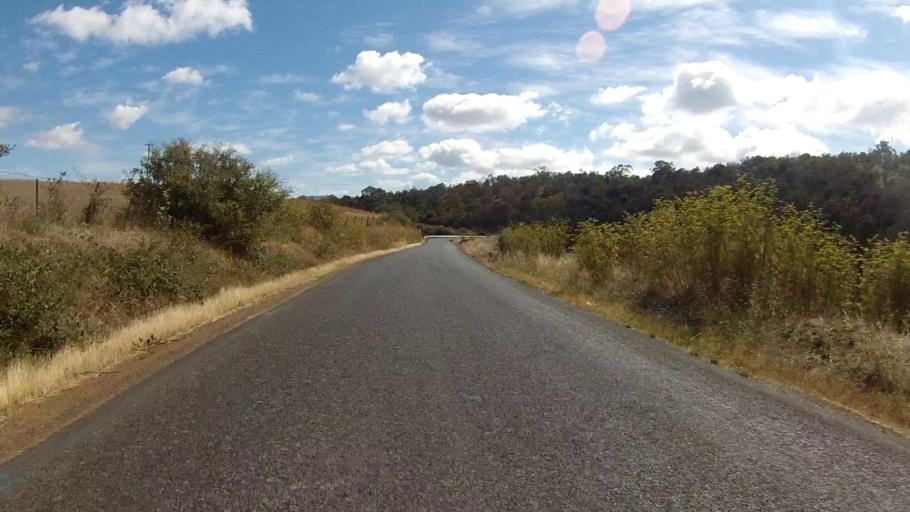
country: AU
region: Tasmania
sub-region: Brighton
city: Bridgewater
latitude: -42.7319
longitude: 147.2612
